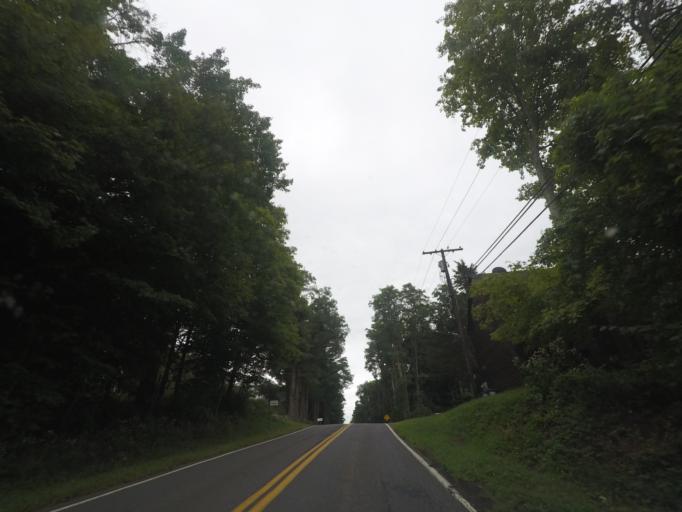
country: US
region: New York
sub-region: Columbia County
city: Chatham
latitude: 42.4430
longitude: -73.5644
